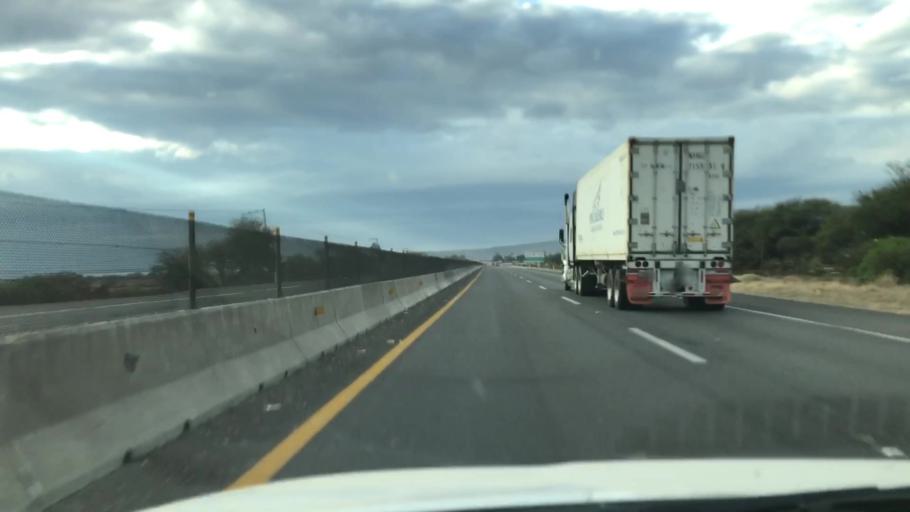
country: MX
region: Guanajuato
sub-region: Penjamo
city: Mezquite de Luna
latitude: 20.3850
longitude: -101.9073
